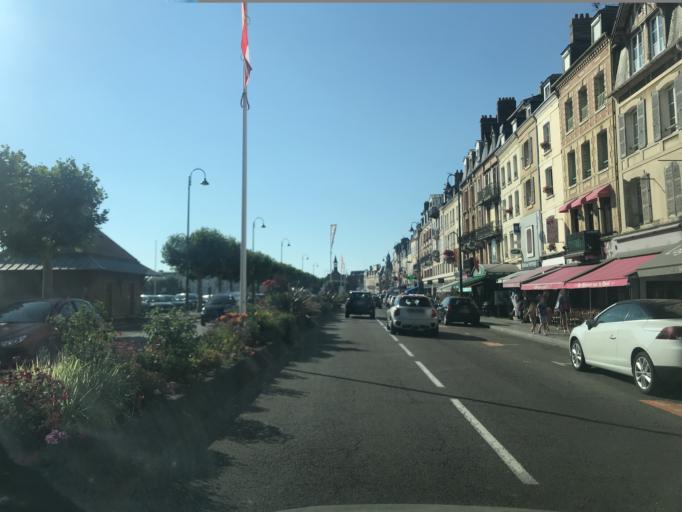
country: FR
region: Lower Normandy
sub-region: Departement du Calvados
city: Trouville-sur-Mer
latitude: 49.3631
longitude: 0.0847
